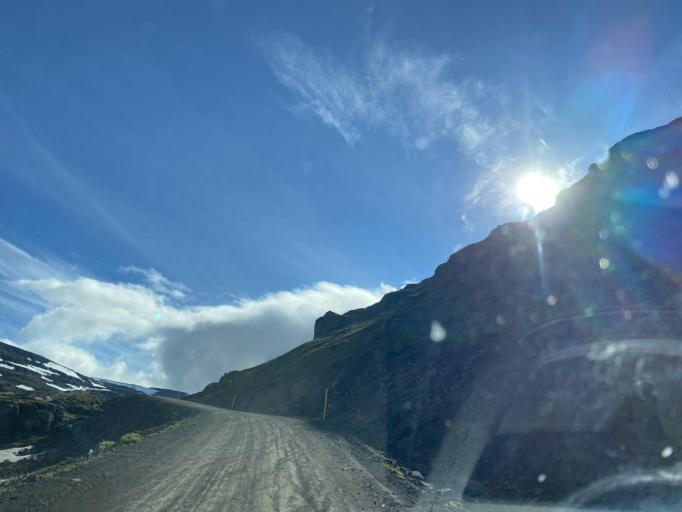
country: IS
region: East
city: Eskifjoerdur
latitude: 65.1752
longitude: -14.1139
